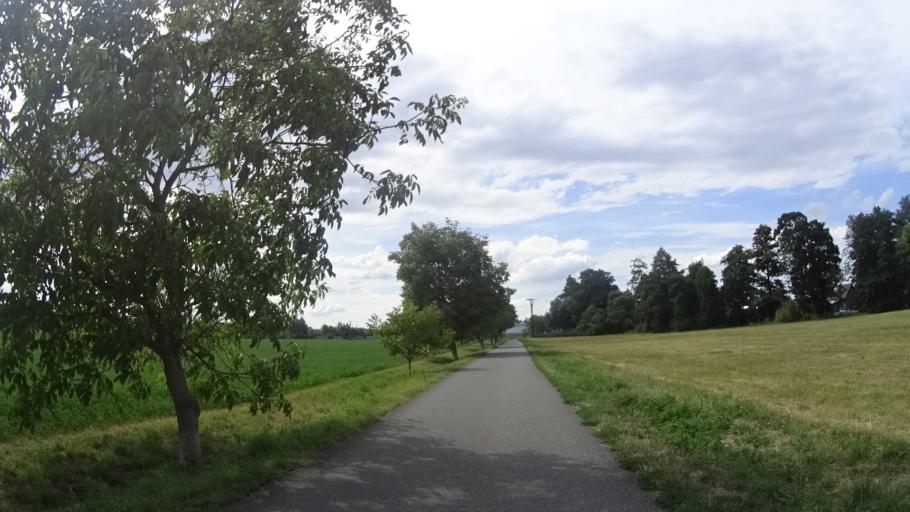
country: CZ
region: Olomoucky
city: Litovel
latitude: 49.6975
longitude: 17.0916
